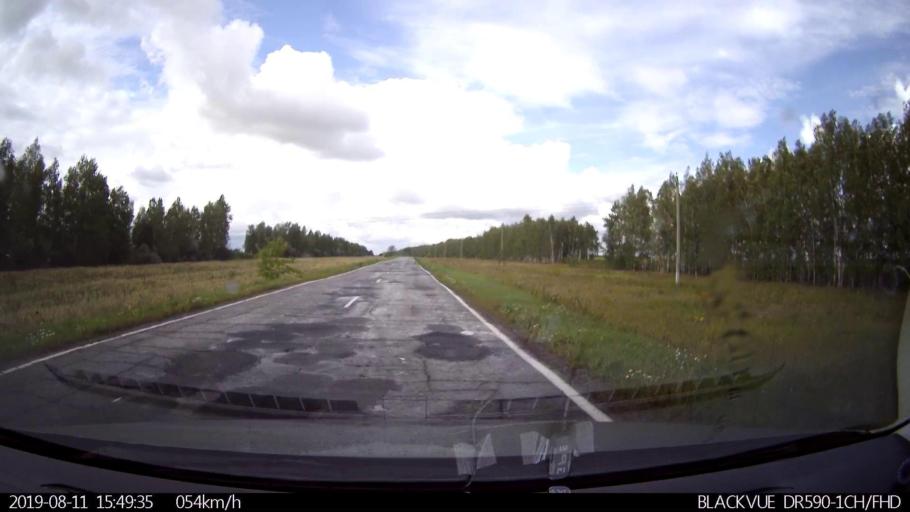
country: RU
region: Ulyanovsk
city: Ignatovka
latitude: 53.9054
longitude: 47.6552
